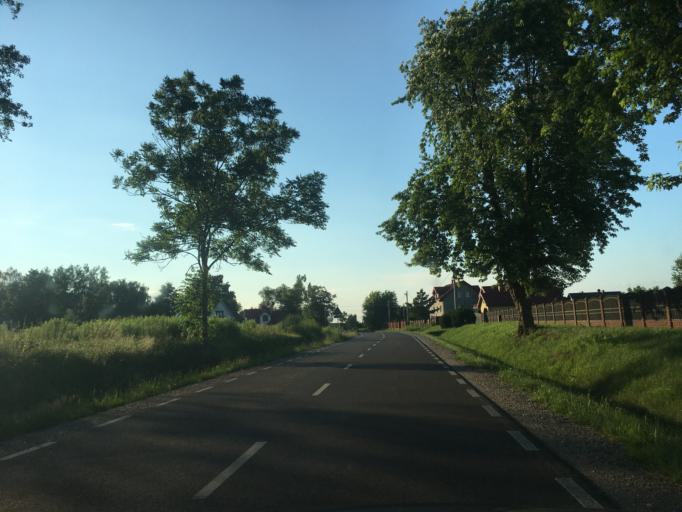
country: PL
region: Masovian Voivodeship
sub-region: Powiat warszawski zachodni
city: Bieniewice
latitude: 52.1218
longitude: 20.5660
